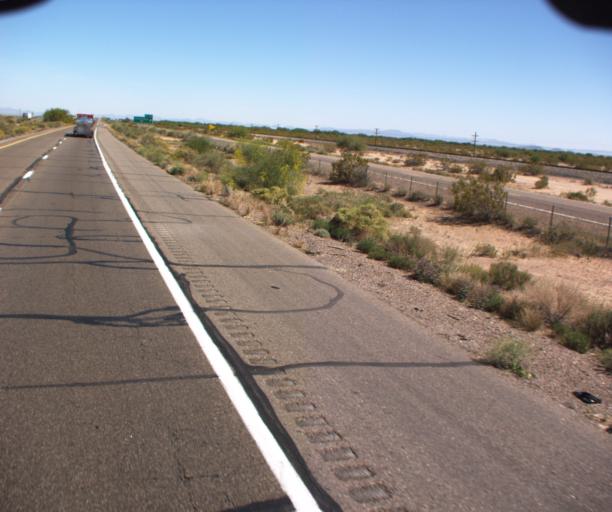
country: US
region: Arizona
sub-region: Maricopa County
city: Gila Bend
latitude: 32.9102
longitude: -112.9676
